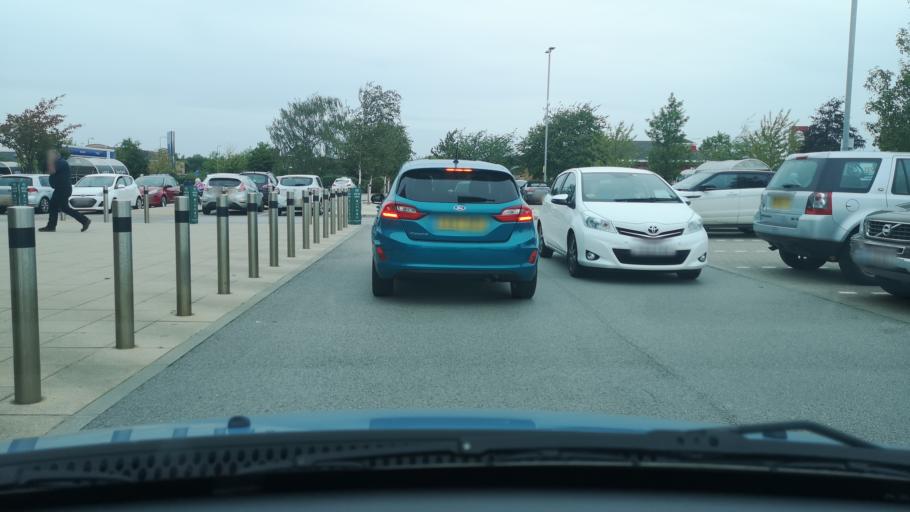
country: GB
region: England
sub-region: North Lincolnshire
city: Gunness
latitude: 53.5886
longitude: -0.6924
